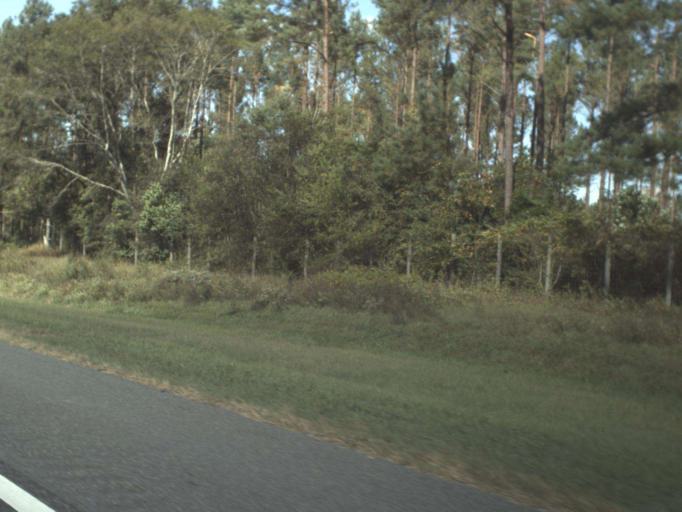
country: US
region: Florida
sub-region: Jackson County
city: Marianna
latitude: 30.7575
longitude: -85.2839
